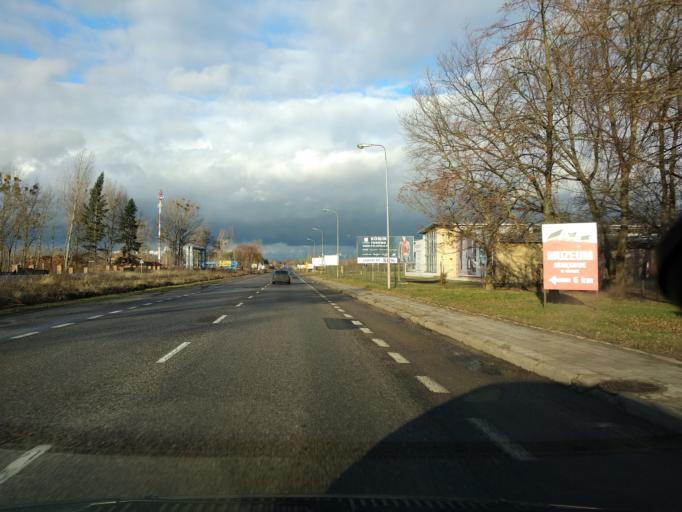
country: PL
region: Greater Poland Voivodeship
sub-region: Konin
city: Konin
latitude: 52.2465
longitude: 18.2701
